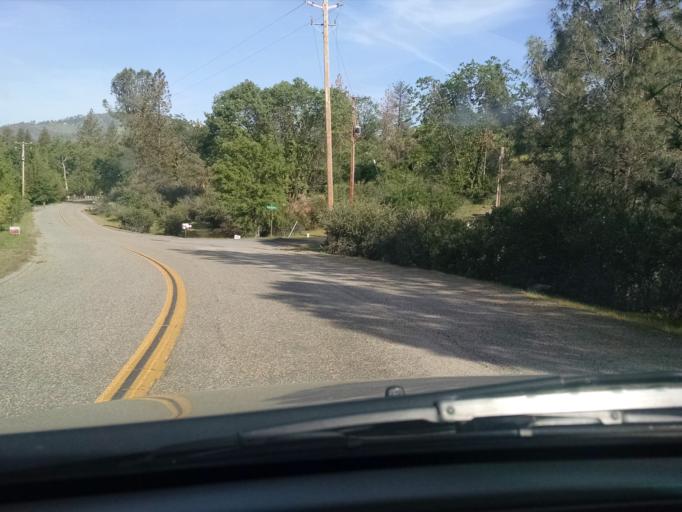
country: US
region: California
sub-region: Madera County
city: Oakhurst
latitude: 37.2875
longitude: -119.6255
